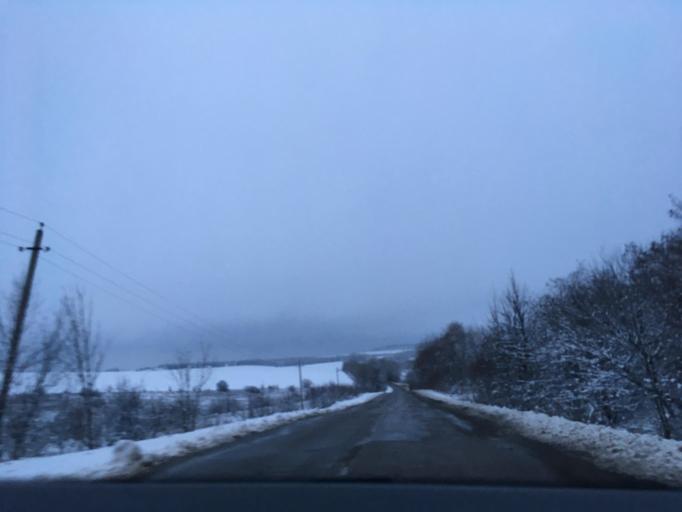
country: RU
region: Voronezj
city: Verkhniy Mamon
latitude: 50.0516
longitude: 40.2467
